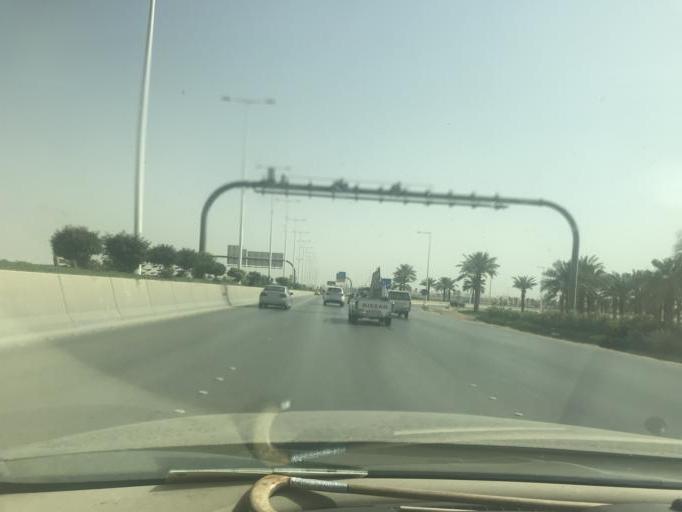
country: SA
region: Ar Riyad
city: Riyadh
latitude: 24.7303
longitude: 46.7094
